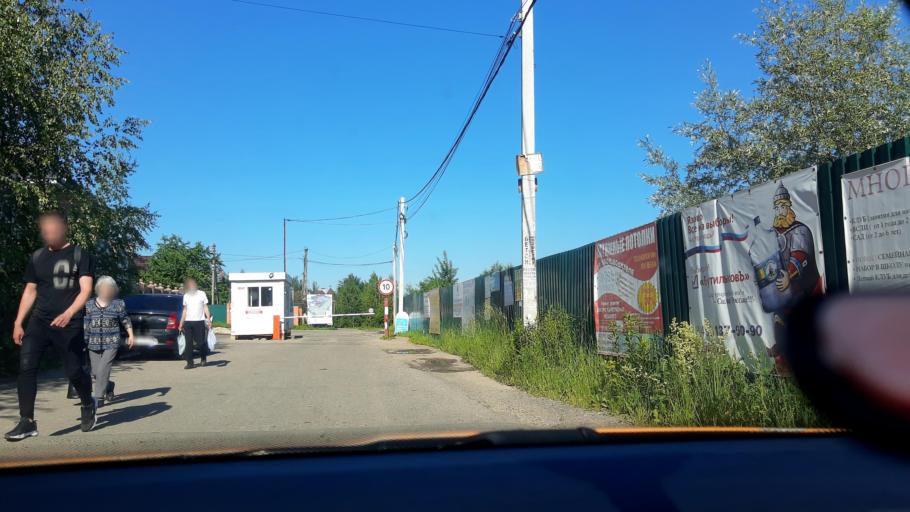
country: RU
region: Moskovskaya
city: Kommunarka
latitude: 55.5263
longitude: 37.5017
